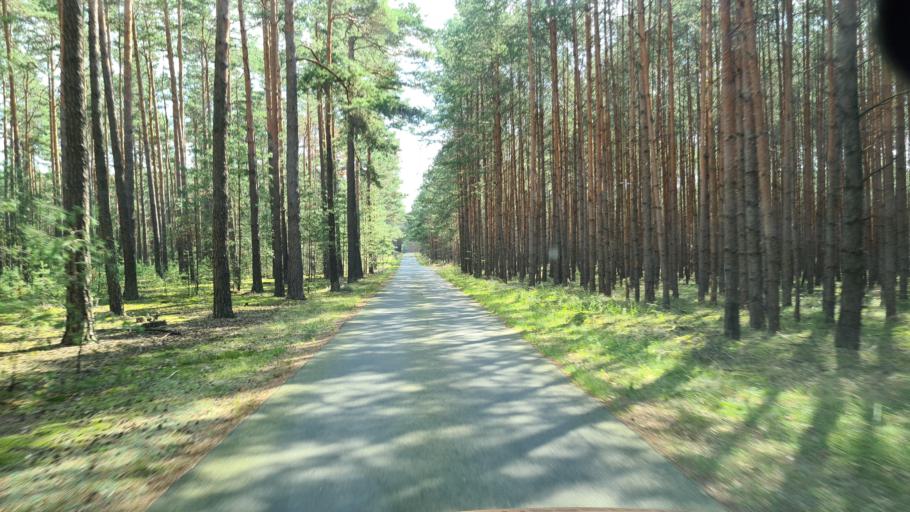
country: DE
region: Brandenburg
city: Sonnewalde
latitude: 51.7818
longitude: 13.5973
